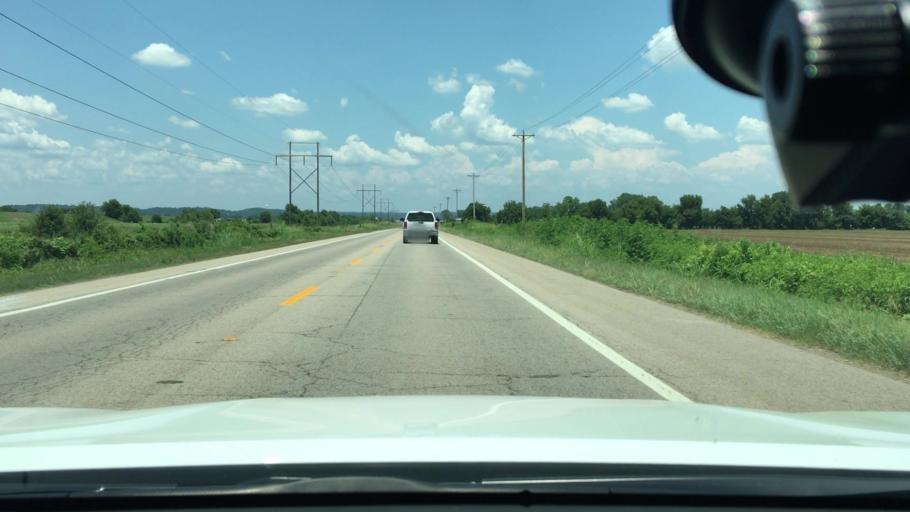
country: US
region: Arkansas
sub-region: Crawford County
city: Van Buren
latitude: 35.3970
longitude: -94.3303
